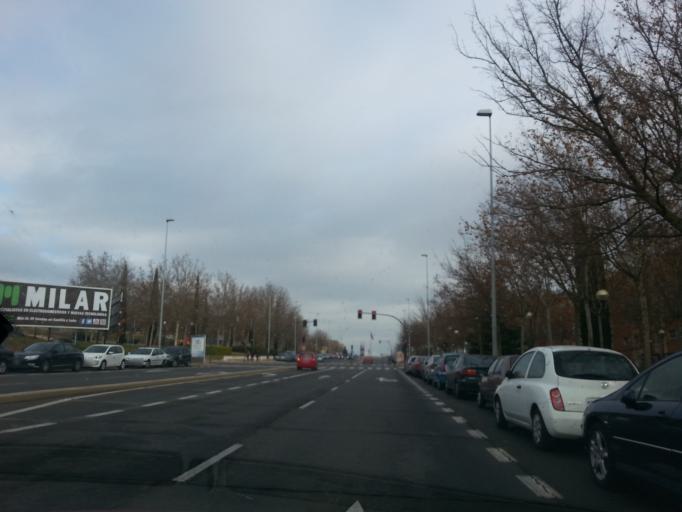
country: ES
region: Castille and Leon
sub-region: Provincia de Salamanca
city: Salamanca
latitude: 40.9754
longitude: -5.6692
